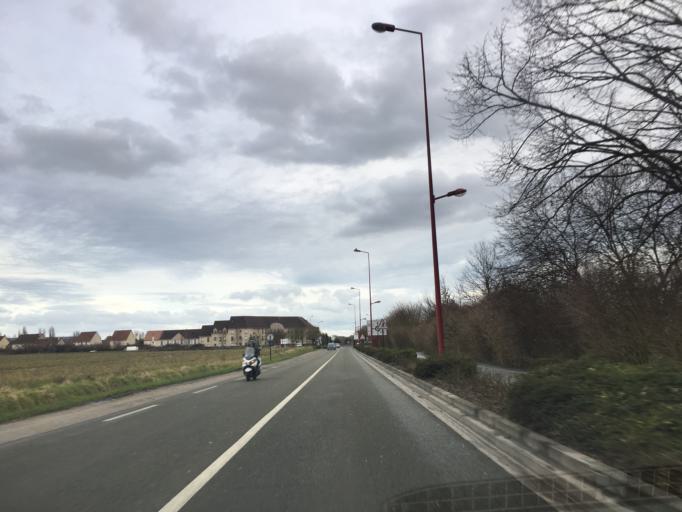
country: FR
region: Ile-de-France
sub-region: Departement du Val-d'Oise
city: Gonesse
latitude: 48.9946
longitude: 2.4405
